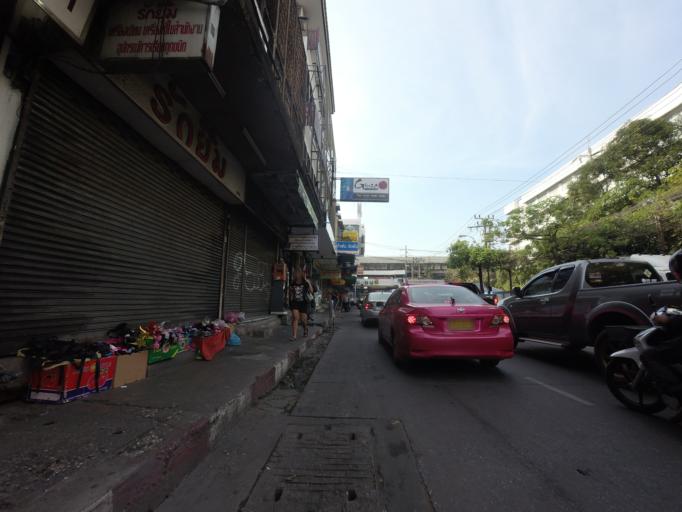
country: TH
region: Bangkok
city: Wang Thonglang
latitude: 13.7547
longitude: 100.6142
